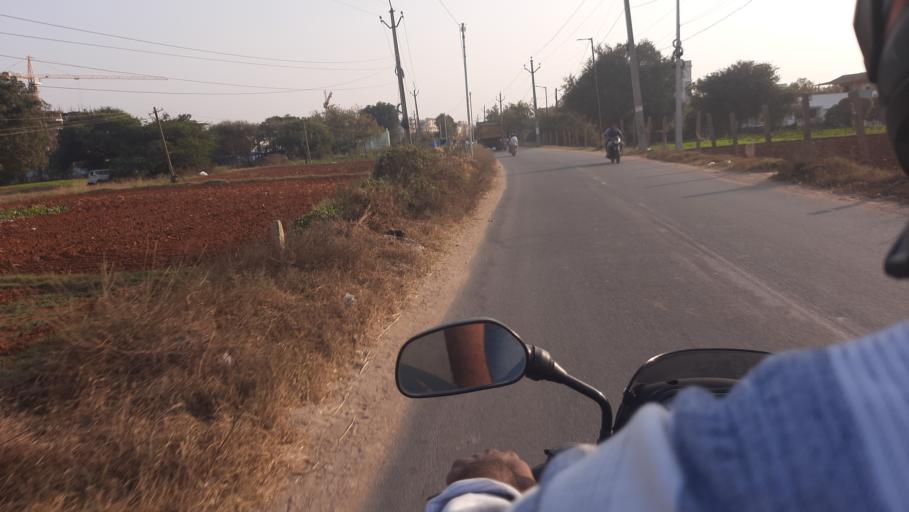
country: IN
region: Telangana
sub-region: Rangareddi
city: Secunderabad
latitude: 17.5248
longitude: 78.5418
